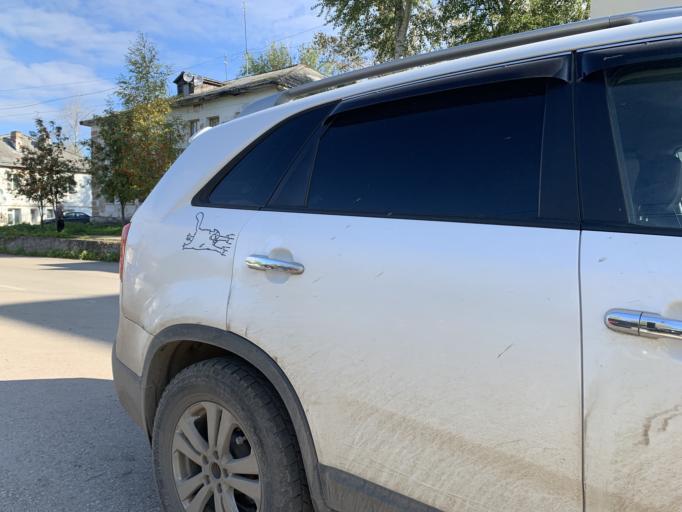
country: RU
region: Perm
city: Gubakha
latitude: 58.8421
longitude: 57.5539
